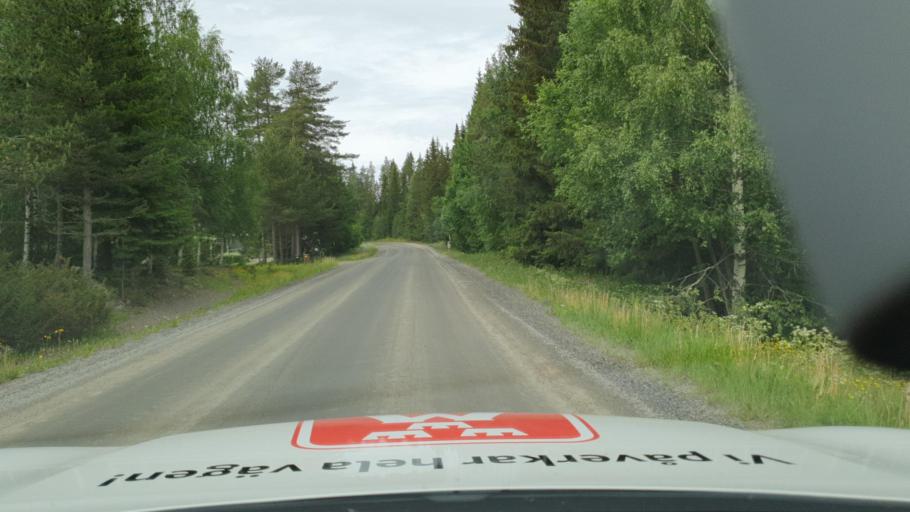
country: SE
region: Vaesterbotten
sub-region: Skelleftea Kommun
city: Burtraesk
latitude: 64.3665
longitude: 20.4021
